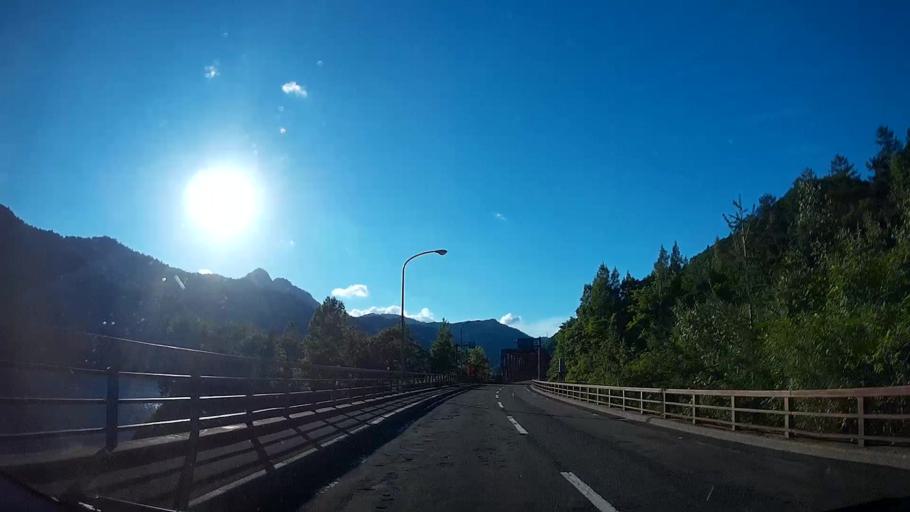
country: JP
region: Hokkaido
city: Sapporo
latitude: 42.9983
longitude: 141.1539
